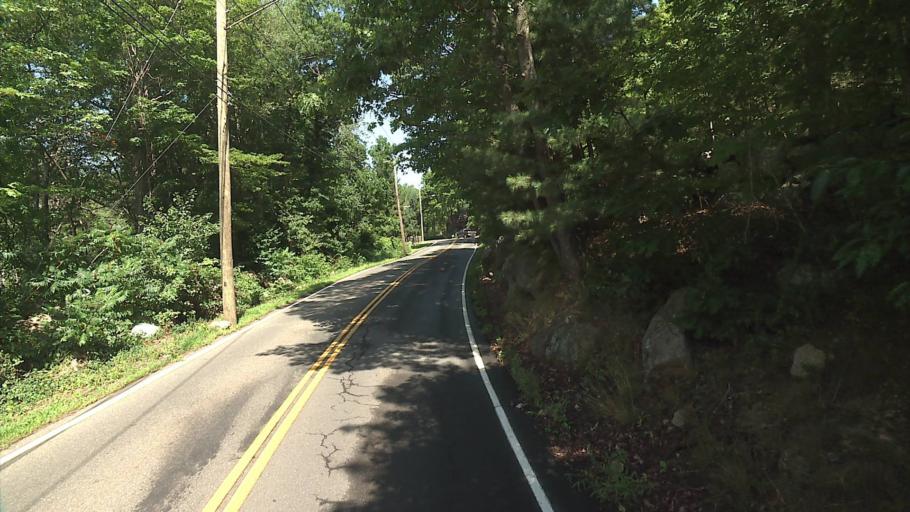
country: US
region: Connecticut
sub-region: New Haven County
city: North Branford
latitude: 41.2732
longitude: -72.7437
